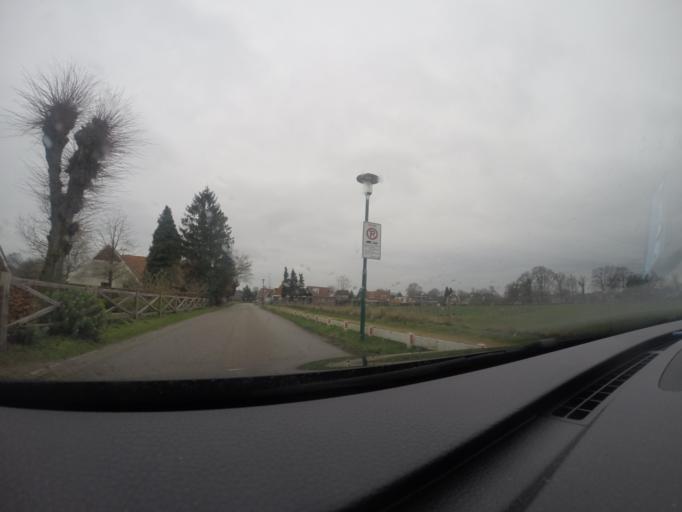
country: NL
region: Overijssel
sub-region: Gemeente Hengelo
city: Hengelo
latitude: 52.2068
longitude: 6.7863
